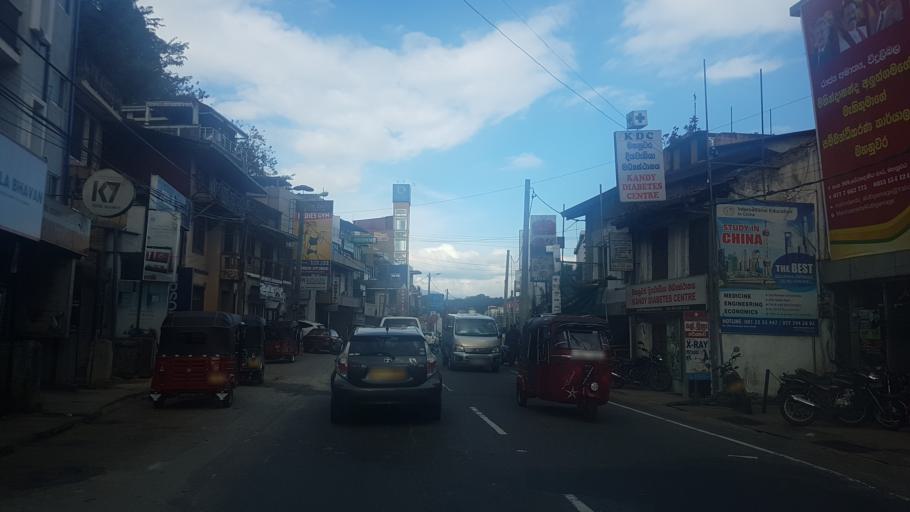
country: LK
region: Central
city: Kandy
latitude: 7.2879
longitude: 80.6284
